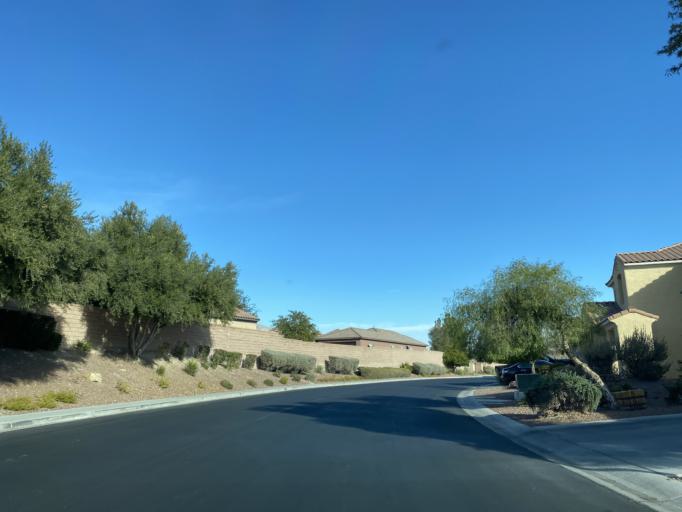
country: US
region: Nevada
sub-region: Clark County
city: North Las Vegas
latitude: 36.3202
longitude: -115.2509
